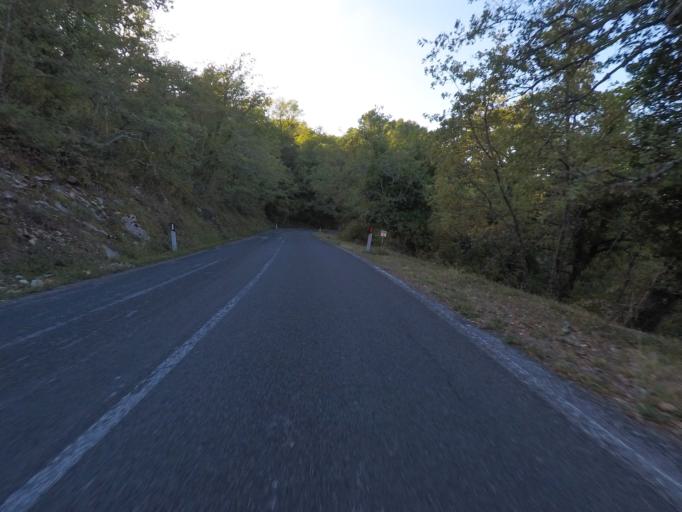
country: IT
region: Tuscany
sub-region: Provincia di Siena
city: Radda in Chianti
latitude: 43.4615
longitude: 11.3851
